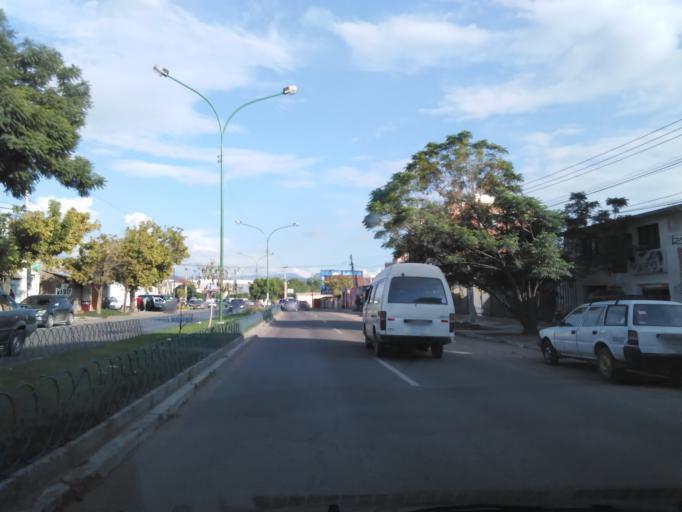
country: BO
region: Cochabamba
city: Cochabamba
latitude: -17.3635
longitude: -66.1801
